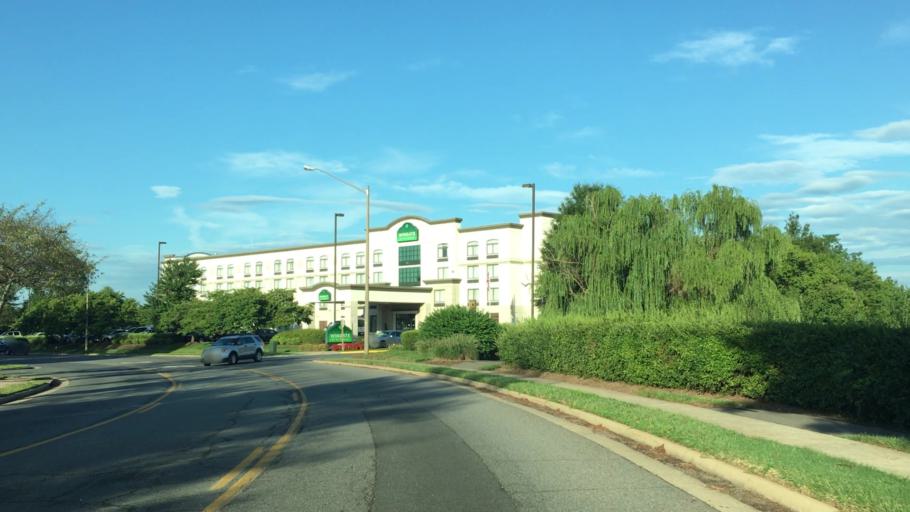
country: US
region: Virginia
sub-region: Fairfax County
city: Chantilly
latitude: 38.8977
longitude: -77.4317
